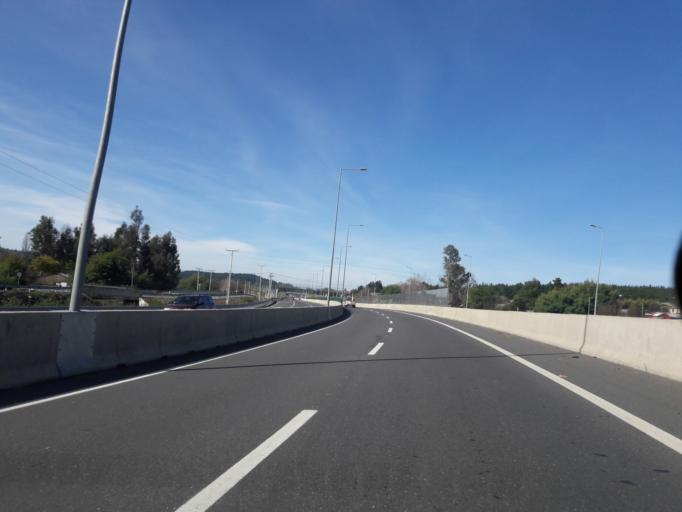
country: CL
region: Biobio
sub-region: Provincia de Biobio
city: Yumbel
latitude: -36.9851
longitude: -72.6267
